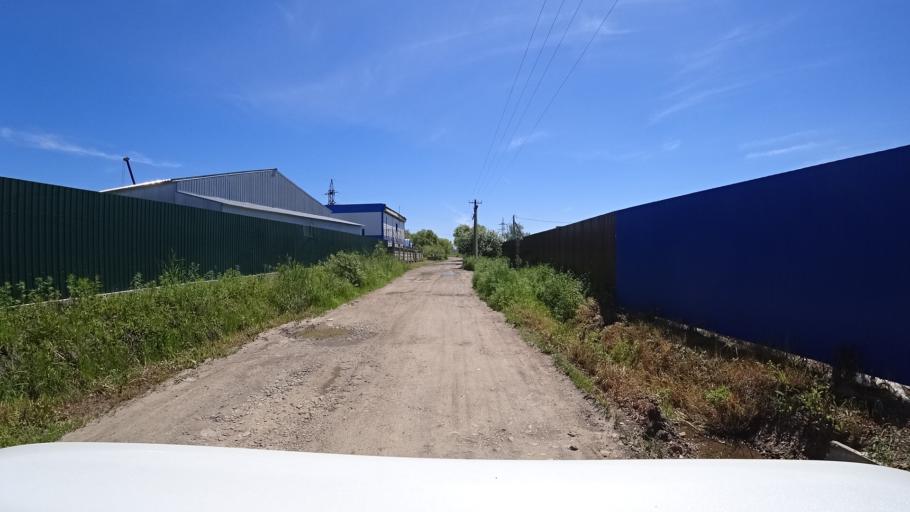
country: RU
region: Khabarovsk Krai
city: Topolevo
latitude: 48.5005
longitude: 135.1823
